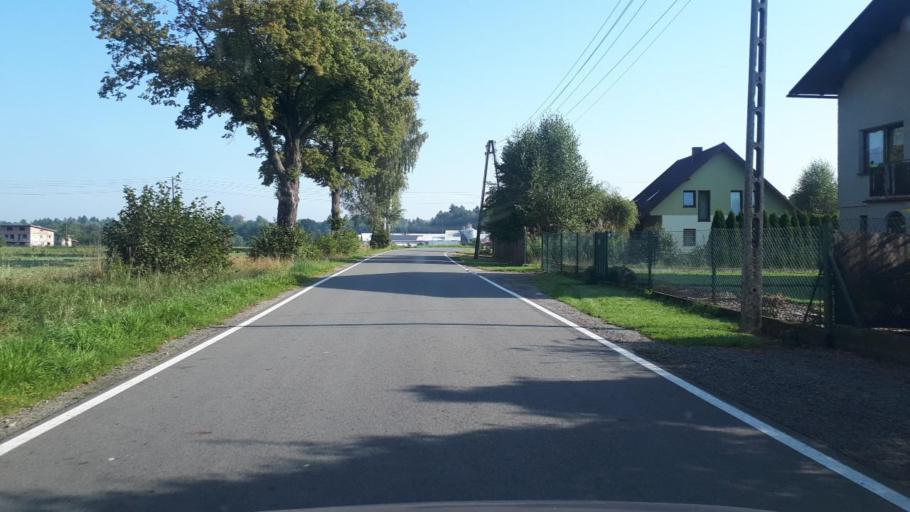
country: PL
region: Silesian Voivodeship
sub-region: Powiat cieszynski
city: Piersciec
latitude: 49.8463
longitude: 18.8321
